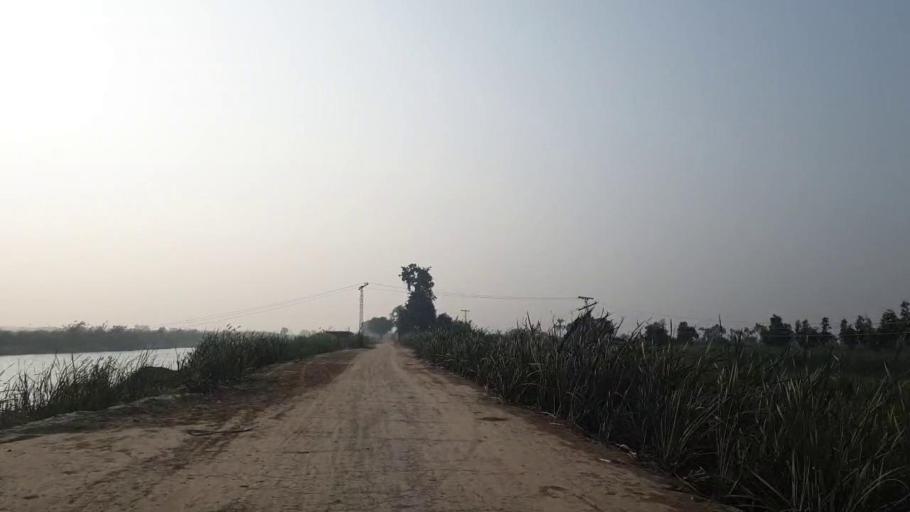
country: PK
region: Sindh
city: Tando Muhammad Khan
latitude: 25.1170
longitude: 68.5670
